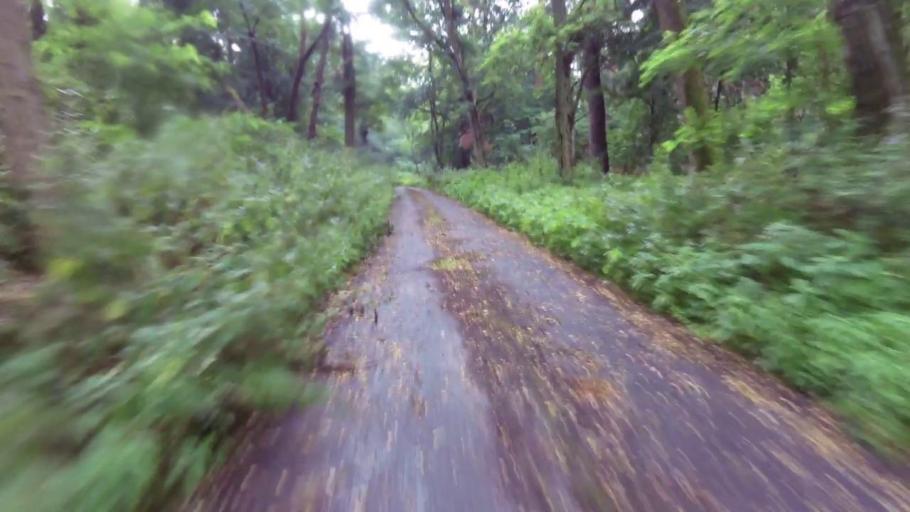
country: PL
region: West Pomeranian Voivodeship
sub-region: Powiat choszczenski
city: Recz
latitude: 53.2450
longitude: 15.4632
